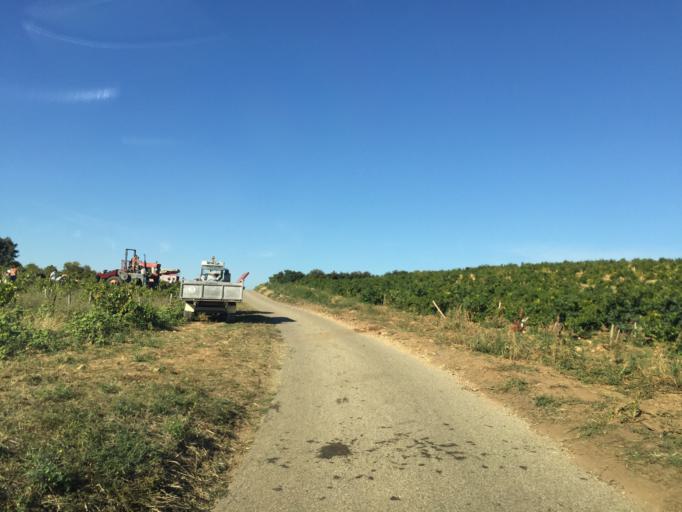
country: FR
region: Provence-Alpes-Cote d'Azur
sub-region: Departement du Vaucluse
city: Chateauneuf-du-Pape
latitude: 44.0601
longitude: 4.8565
